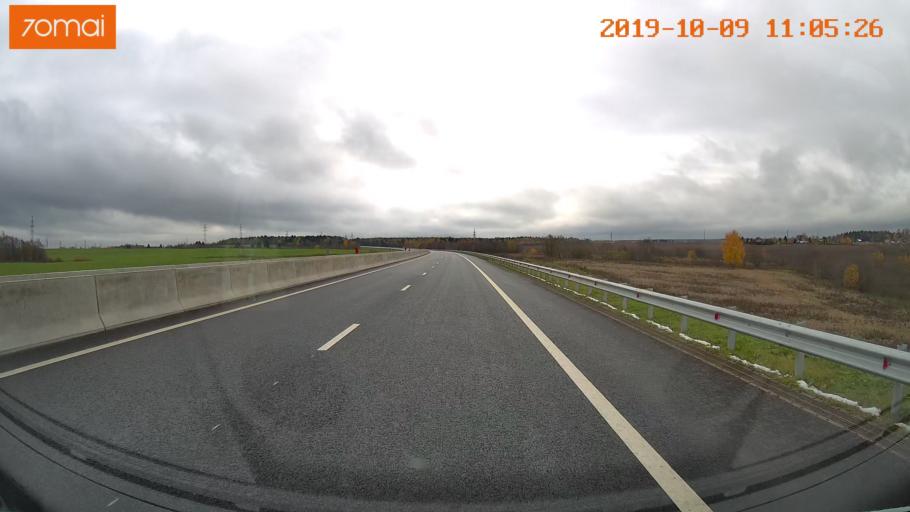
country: RU
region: Vologda
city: Molochnoye
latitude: 59.1999
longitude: 39.7592
